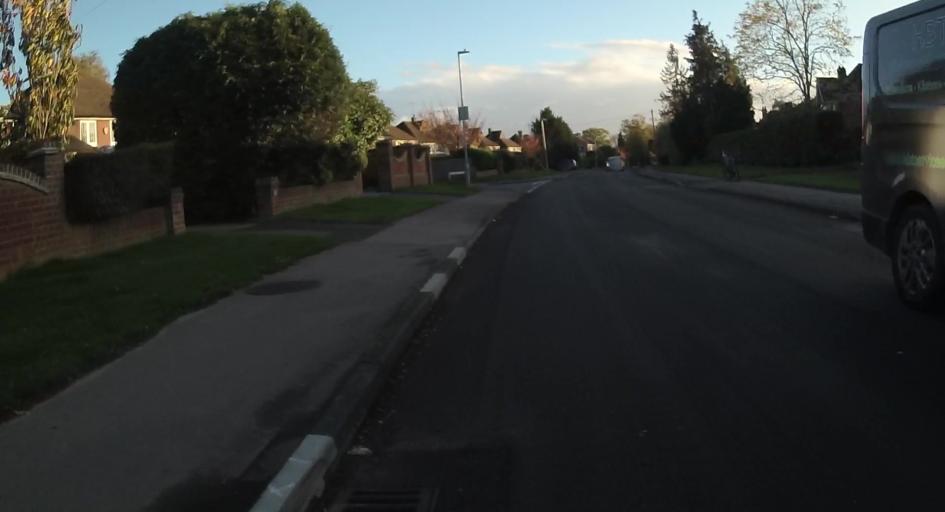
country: GB
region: England
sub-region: Wokingham
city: Wokingham
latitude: 51.4085
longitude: -0.8183
